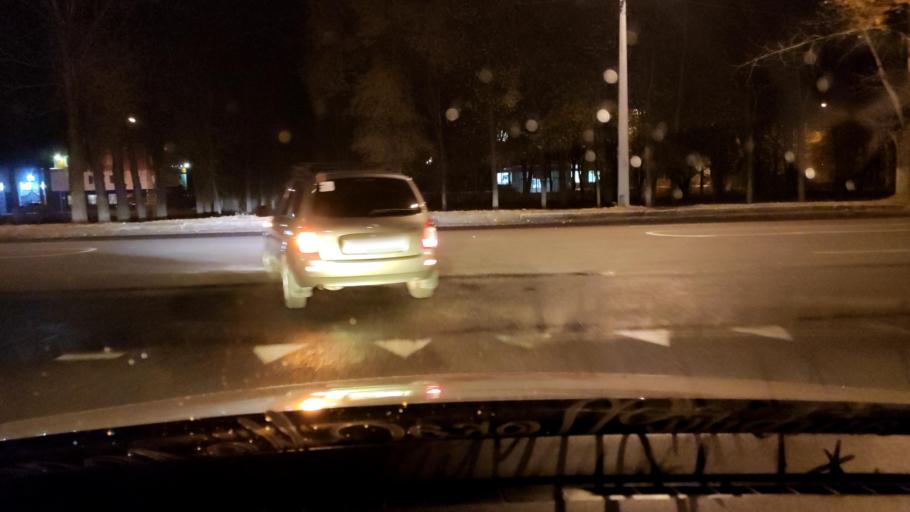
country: RU
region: Voronezj
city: Maslovka
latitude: 51.6087
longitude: 39.2446
